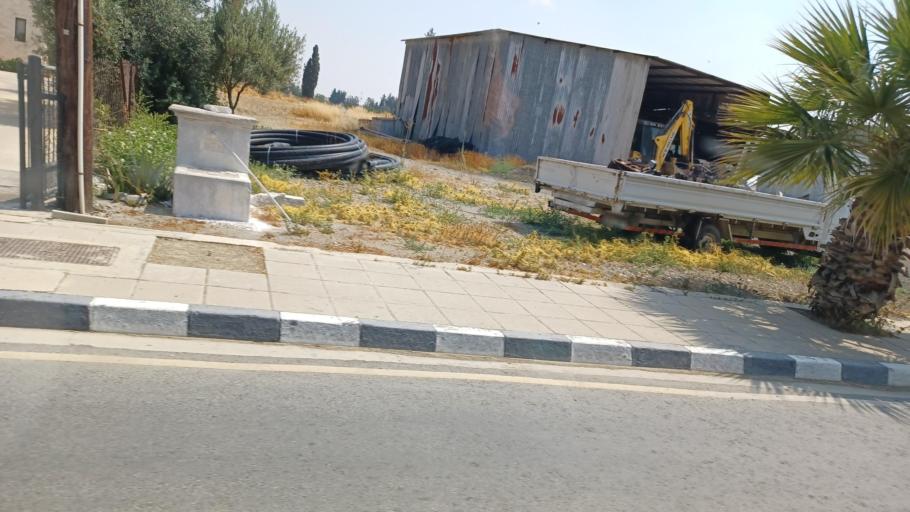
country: CY
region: Lefkosia
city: Dali
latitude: 35.0438
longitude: 33.4443
